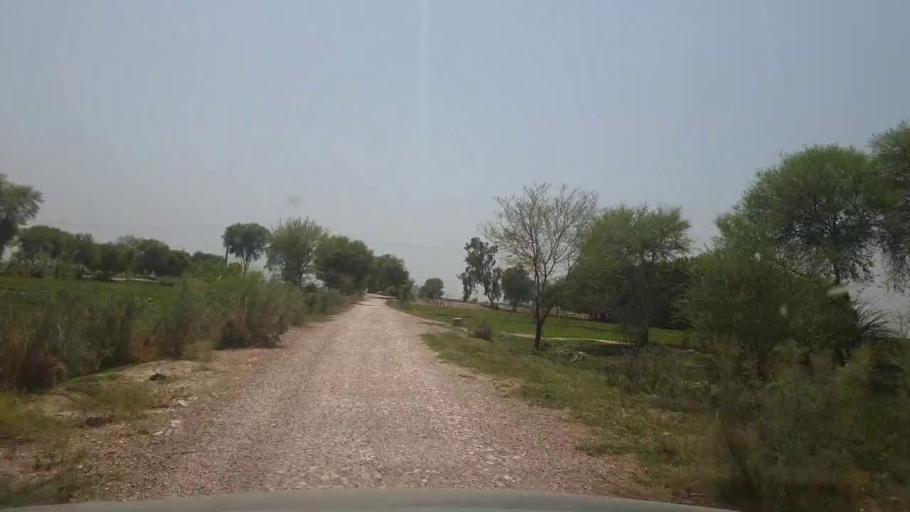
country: PK
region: Sindh
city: Lakhi
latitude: 27.8464
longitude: 68.6642
